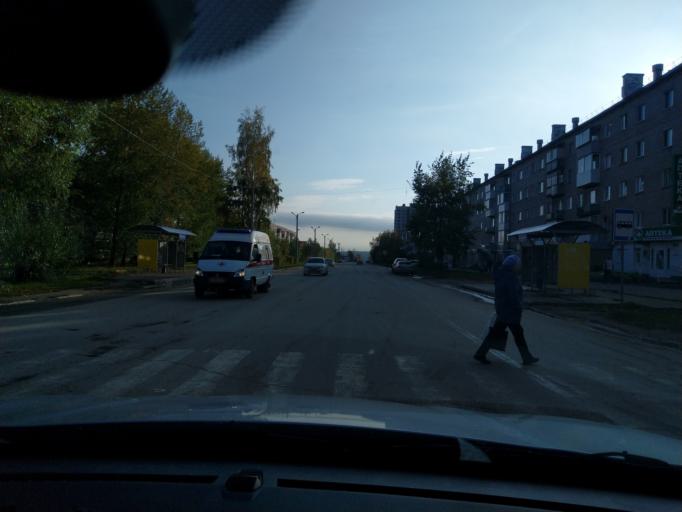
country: RU
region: Perm
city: Dobryanka
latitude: 58.4662
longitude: 56.4026
